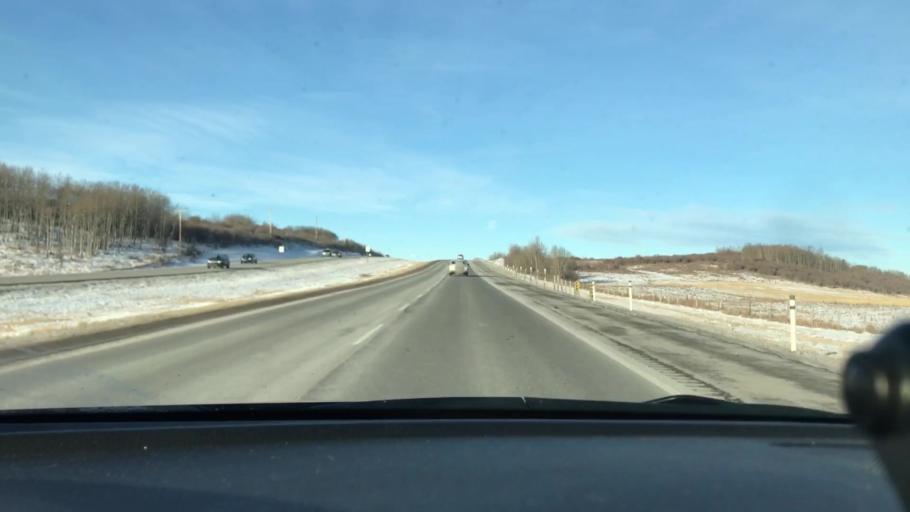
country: CA
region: Alberta
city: Cochrane
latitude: 51.0957
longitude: -114.5918
